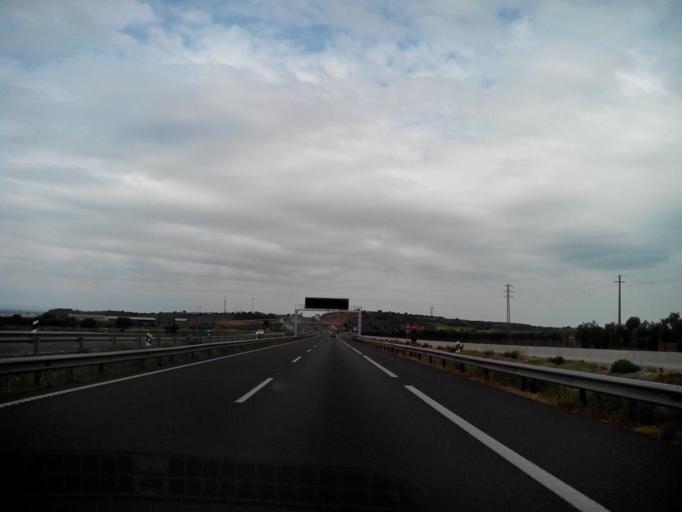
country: ES
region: Catalonia
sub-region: Provincia de Lleida
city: Tarrega
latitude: 41.6623
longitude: 1.1969
